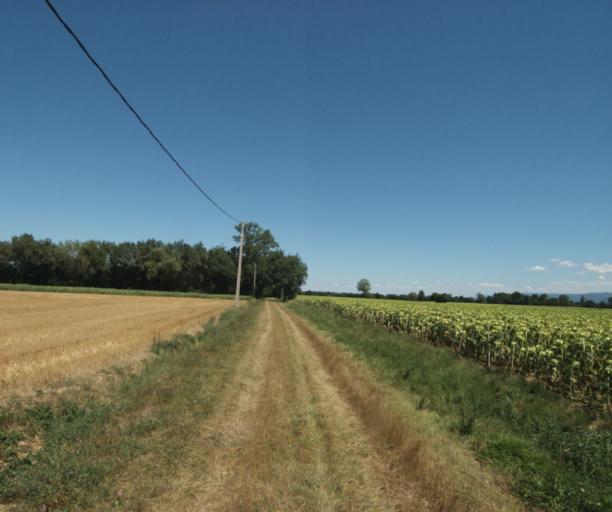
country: FR
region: Midi-Pyrenees
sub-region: Departement de la Haute-Garonne
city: Saint-Felix-Lauragais
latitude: 43.4824
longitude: 1.9435
